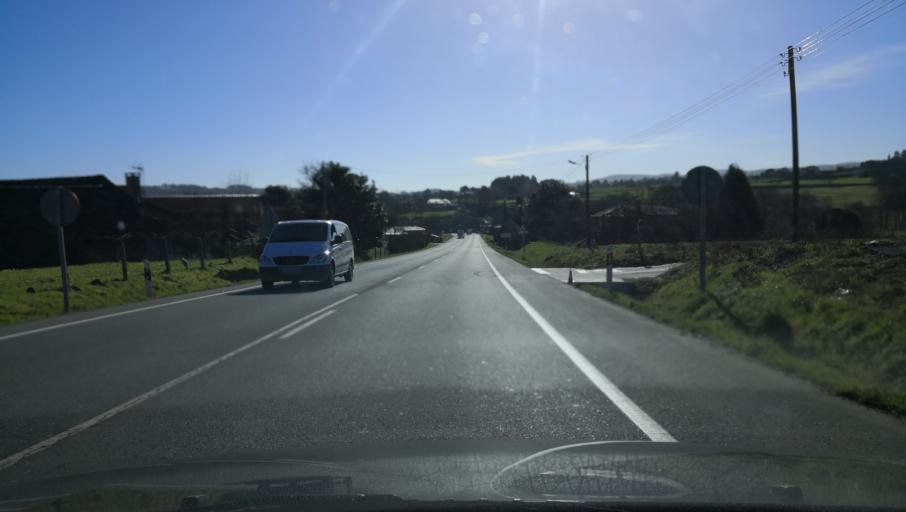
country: ES
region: Galicia
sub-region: Provincia de Pontevedra
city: Silleda
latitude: 42.7258
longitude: -8.2984
